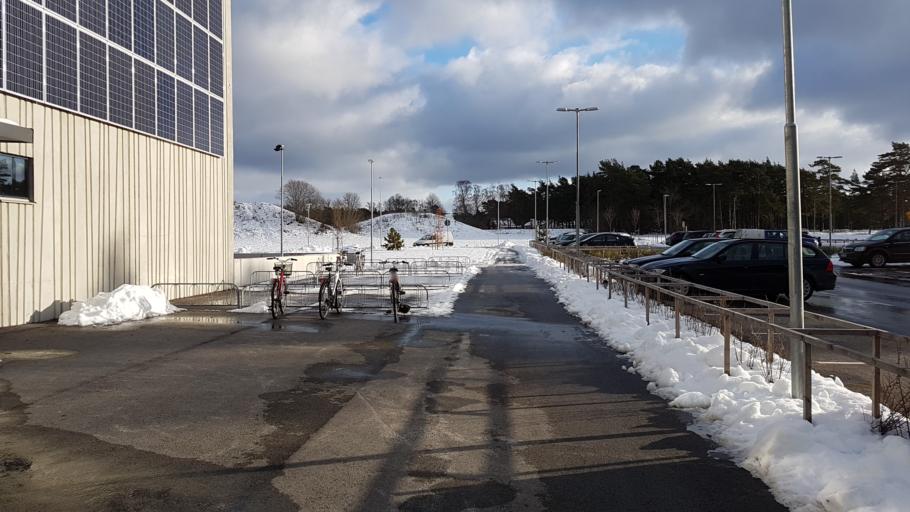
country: SE
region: Gotland
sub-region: Gotland
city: Vibble
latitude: 57.6064
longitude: 18.2811
